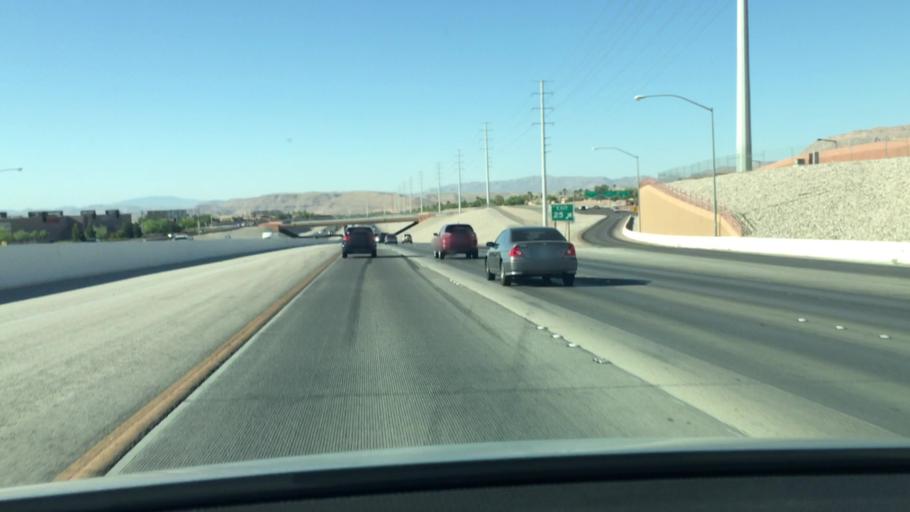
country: US
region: Nevada
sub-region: Clark County
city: Summerlin South
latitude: 36.1489
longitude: -115.3370
